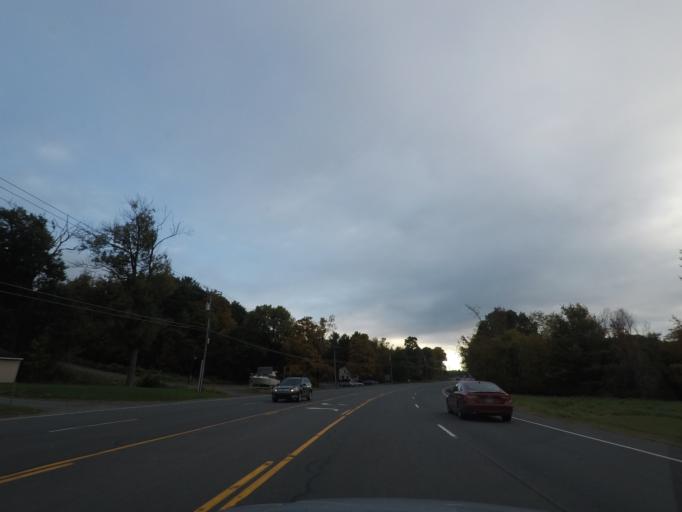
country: US
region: New York
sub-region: Rensselaer County
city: East Greenbush
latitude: 42.5465
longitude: -73.6719
